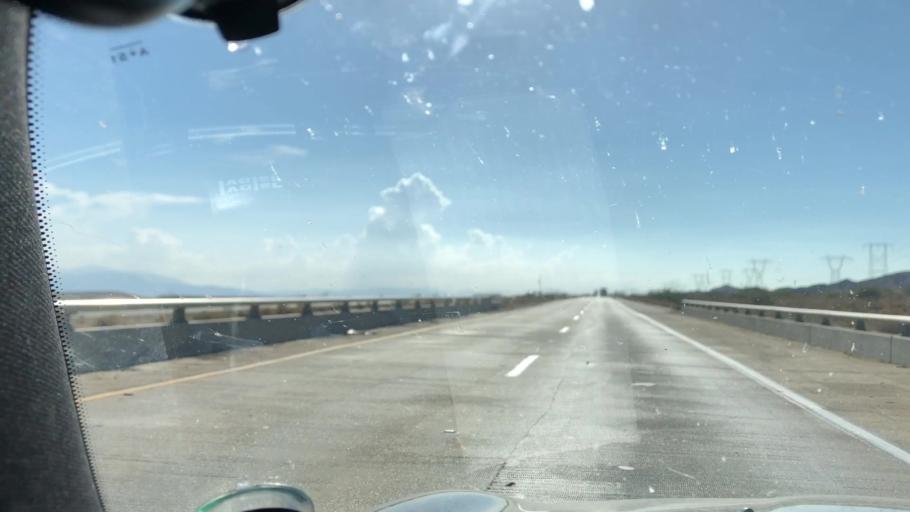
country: US
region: California
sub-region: Riverside County
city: Mecca
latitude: 33.6754
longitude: -115.9454
